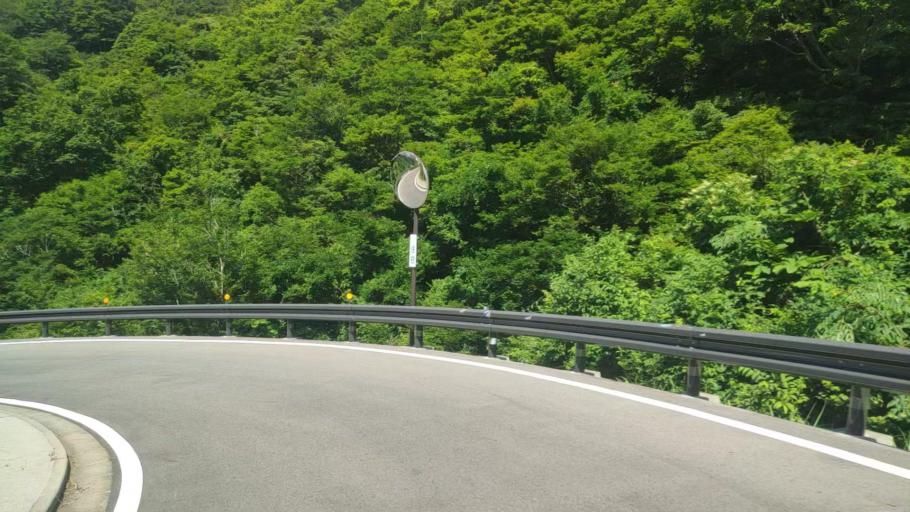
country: JP
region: Fukui
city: Katsuyama
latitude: 36.1492
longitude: 136.5231
